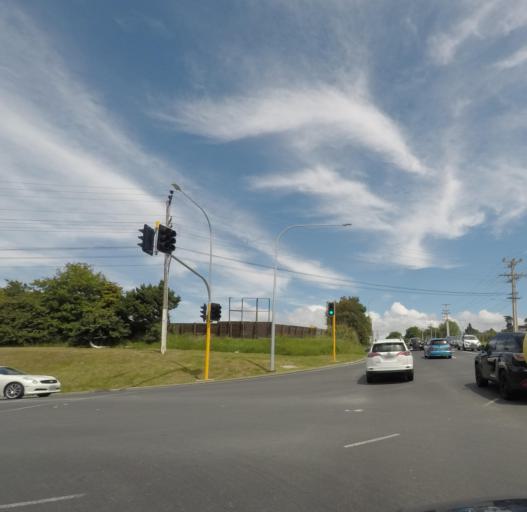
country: NZ
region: Auckland
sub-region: Auckland
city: Rothesay Bay
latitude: -36.6247
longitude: 174.6727
